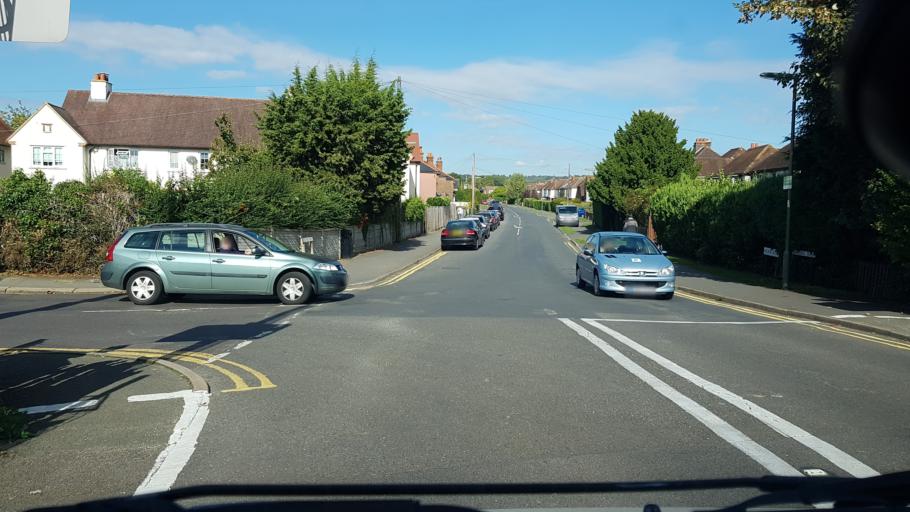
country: GB
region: England
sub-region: Surrey
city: Godalming
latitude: 51.1985
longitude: -0.6024
